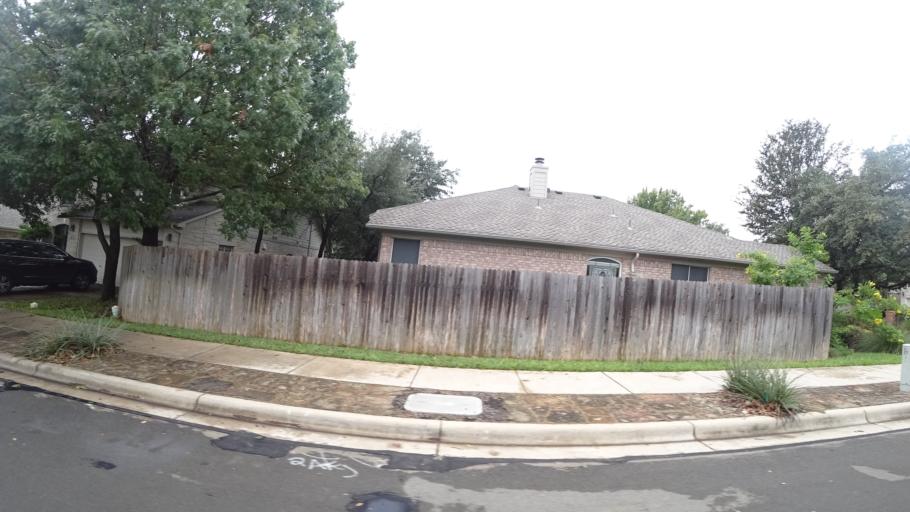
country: US
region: Texas
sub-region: Travis County
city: Shady Hollow
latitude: 30.1887
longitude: -97.8665
